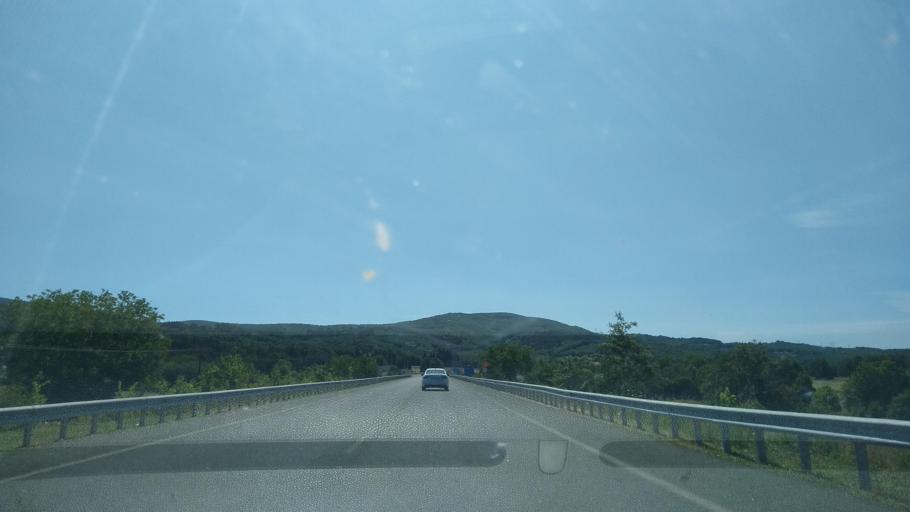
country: GR
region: Central Macedonia
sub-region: Nomos Chalkidikis
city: Palaiochori
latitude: 40.4810
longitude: 23.6409
